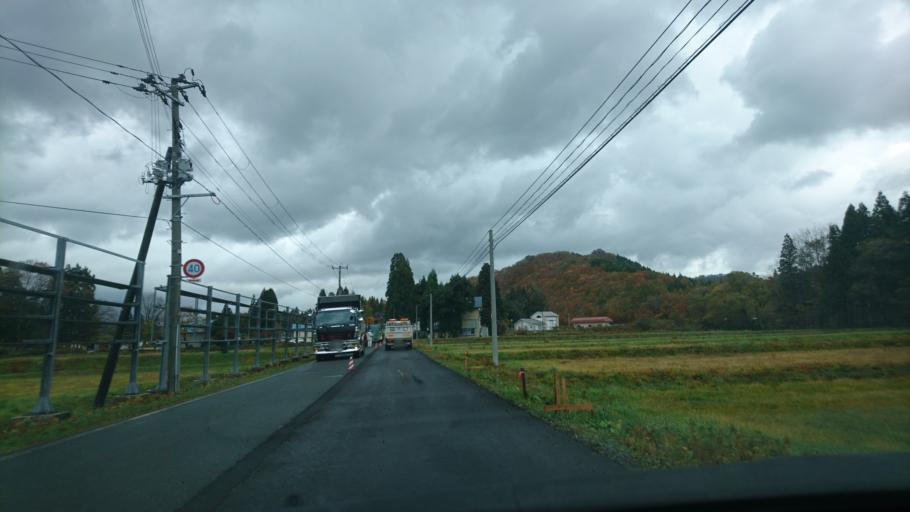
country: JP
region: Iwate
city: Shizukuishi
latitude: 39.5148
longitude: 140.8293
